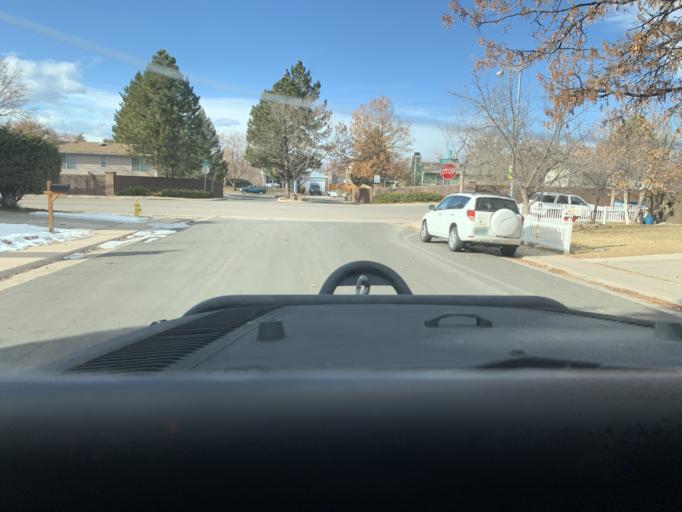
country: US
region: Colorado
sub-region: Adams County
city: Aurora
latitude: 39.7051
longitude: -104.8011
